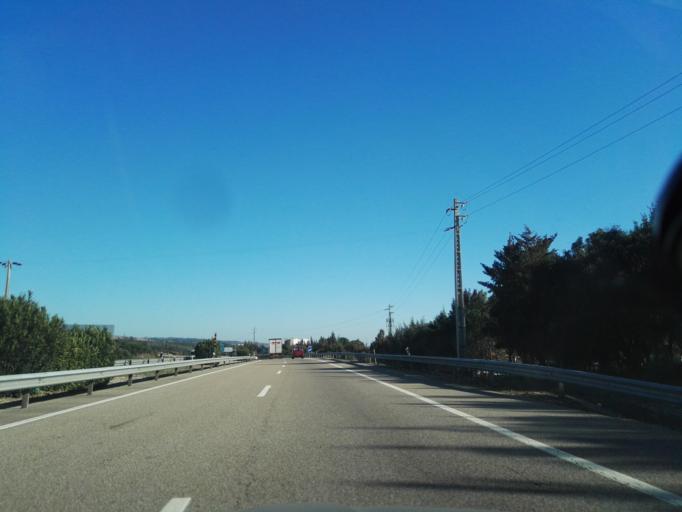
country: PT
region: Santarem
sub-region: Constancia
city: Constancia
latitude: 39.4835
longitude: -8.3339
